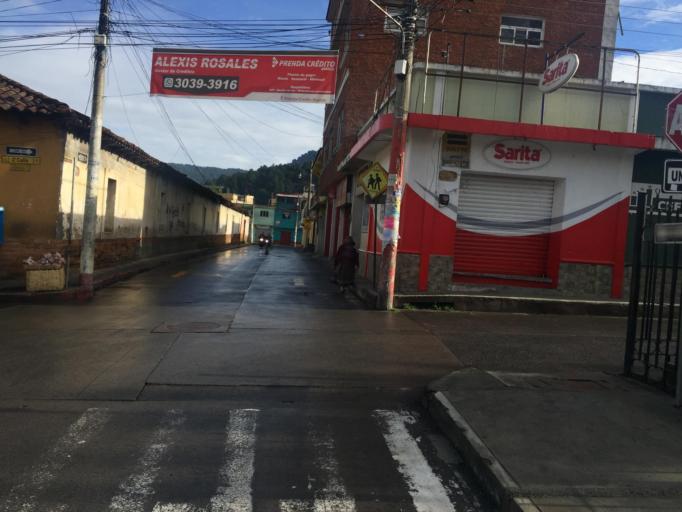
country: GT
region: Totonicapan
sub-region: Municipio de Totonicapan
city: Totonicapan
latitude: 14.9127
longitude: -91.3598
